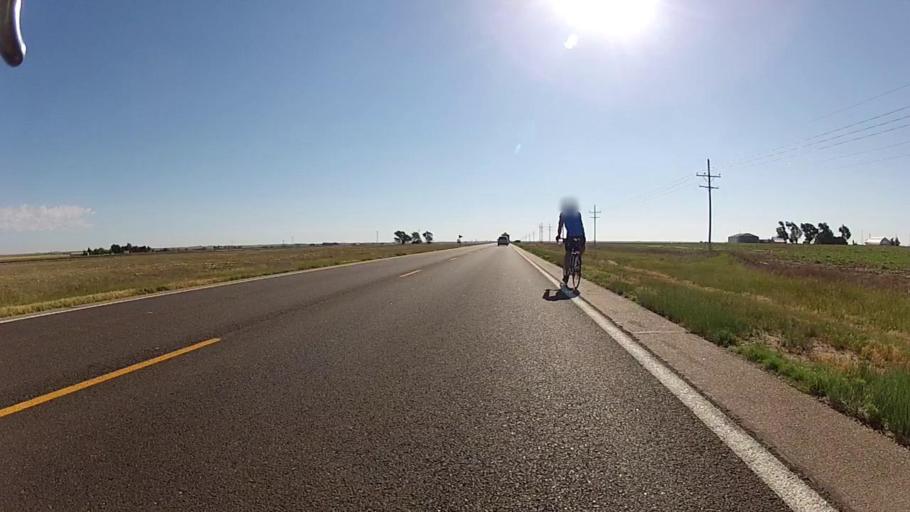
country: US
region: Kansas
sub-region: Haskell County
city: Sublette
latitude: 37.5507
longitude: -100.6009
